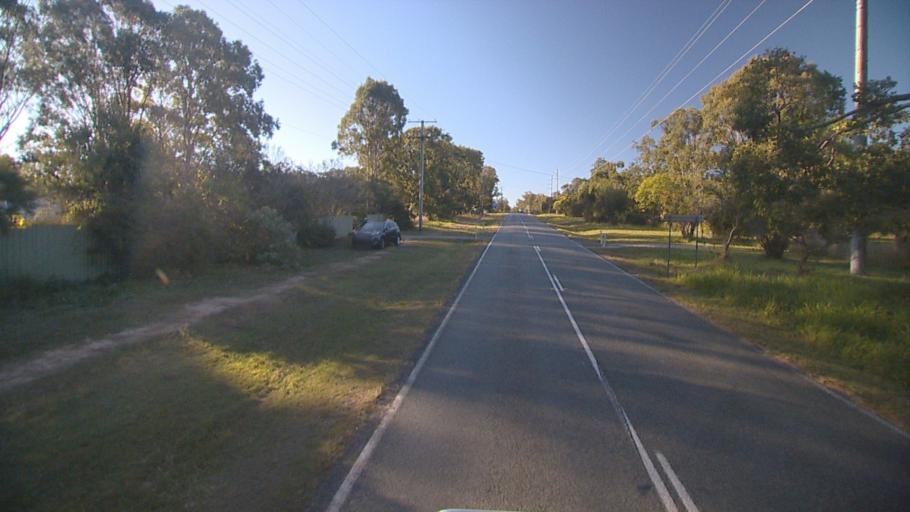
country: AU
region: Queensland
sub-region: Logan
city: Logan Reserve
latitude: -27.7379
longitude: 153.0874
